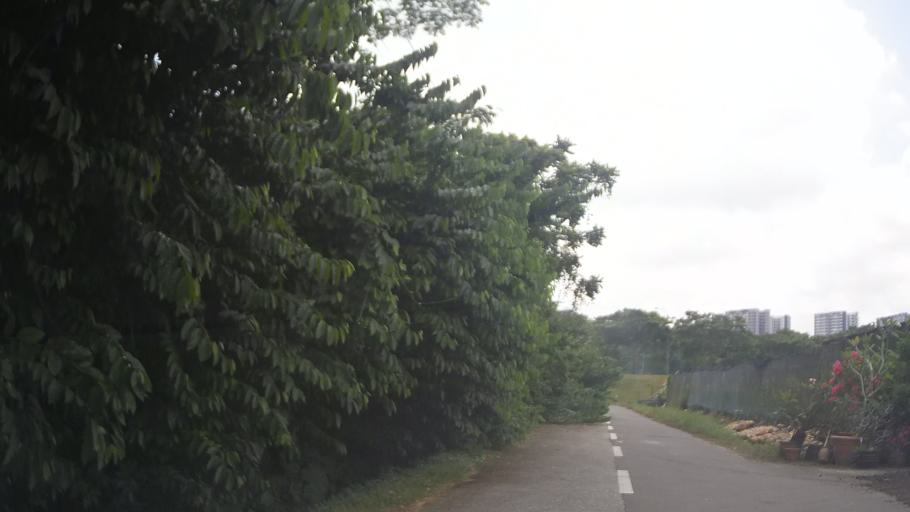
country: MY
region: Johor
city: Kampung Pasir Gudang Baru
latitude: 1.3992
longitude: 103.8678
